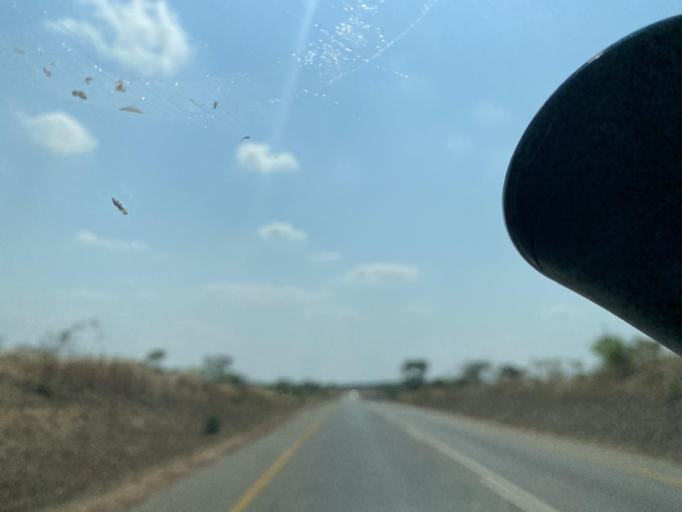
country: ZM
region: Lusaka
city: Chongwe
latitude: -15.5354
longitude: 28.6465
